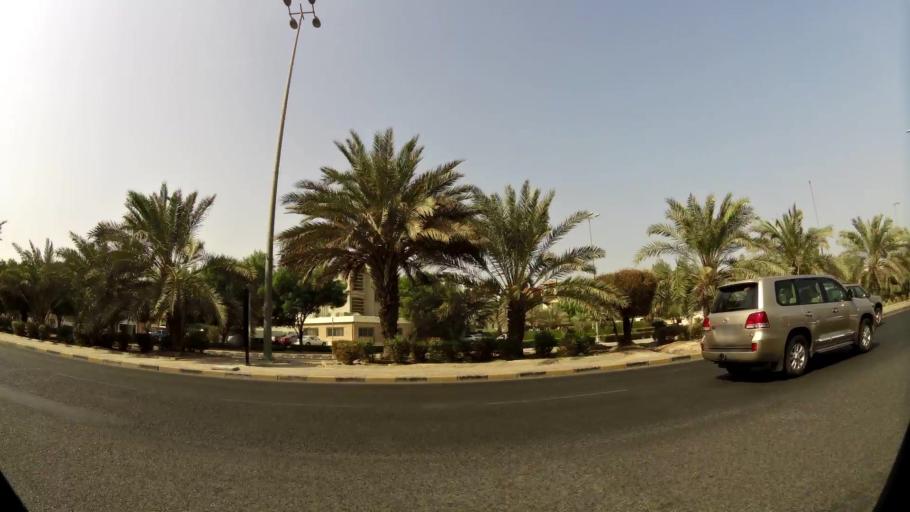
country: KW
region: Al Asimah
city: Ad Dasmah
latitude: 29.3571
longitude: 48.0200
